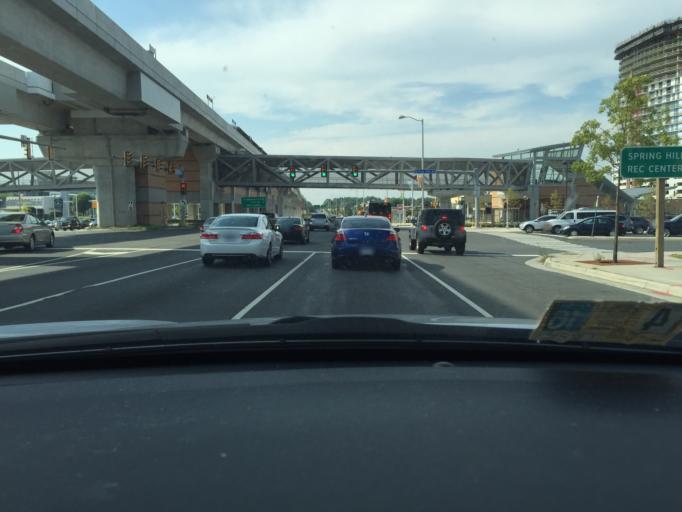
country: US
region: Virginia
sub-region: Fairfax County
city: Tysons Corner
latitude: 38.9282
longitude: -77.2406
